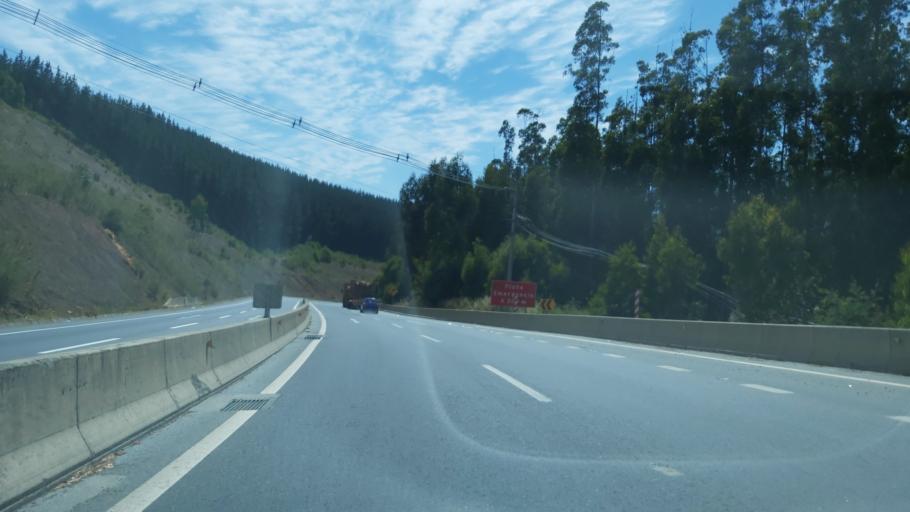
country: CL
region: Biobio
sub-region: Provincia de Concepcion
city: Lota
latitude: -37.1021
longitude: -73.1470
